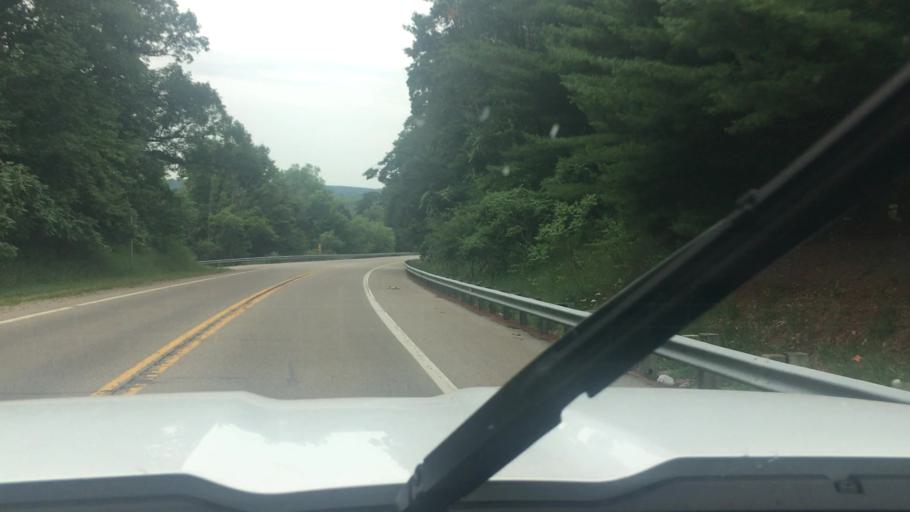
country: US
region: Michigan
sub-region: Ionia County
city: Saranac
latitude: 42.9661
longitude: -85.1477
